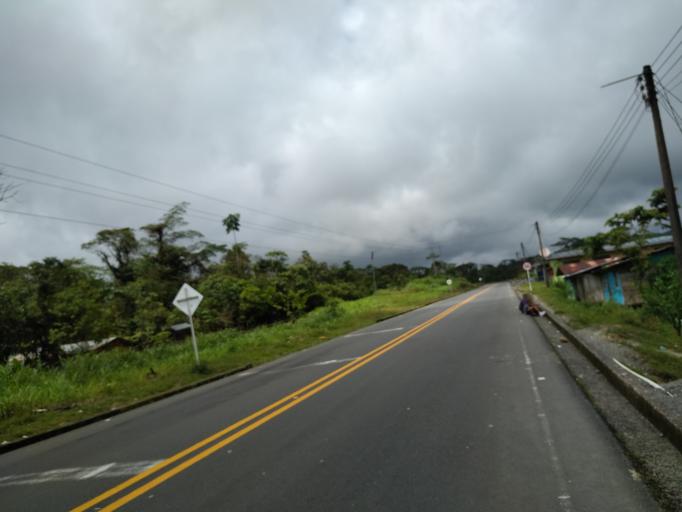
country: CO
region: Narino
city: Ricaurte
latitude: 1.3625
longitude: -78.1797
